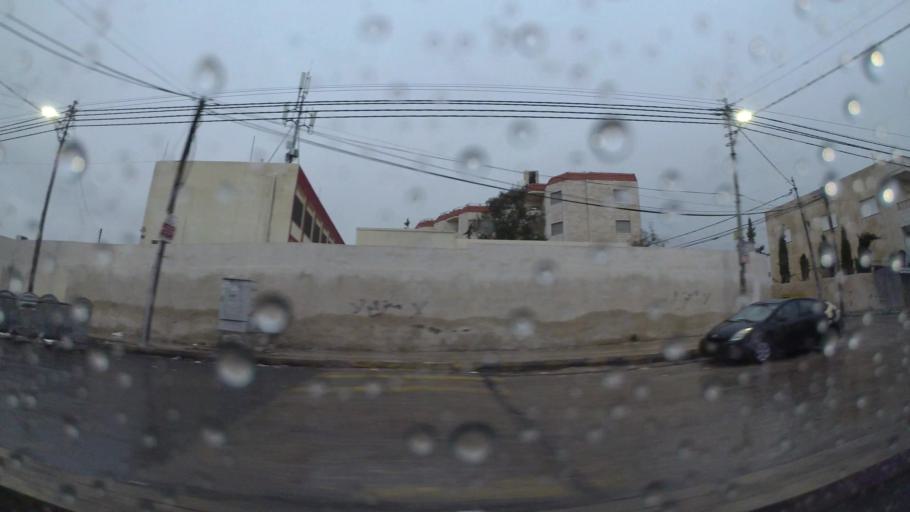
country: JO
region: Amman
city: Amman
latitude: 32.0023
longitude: 35.9653
